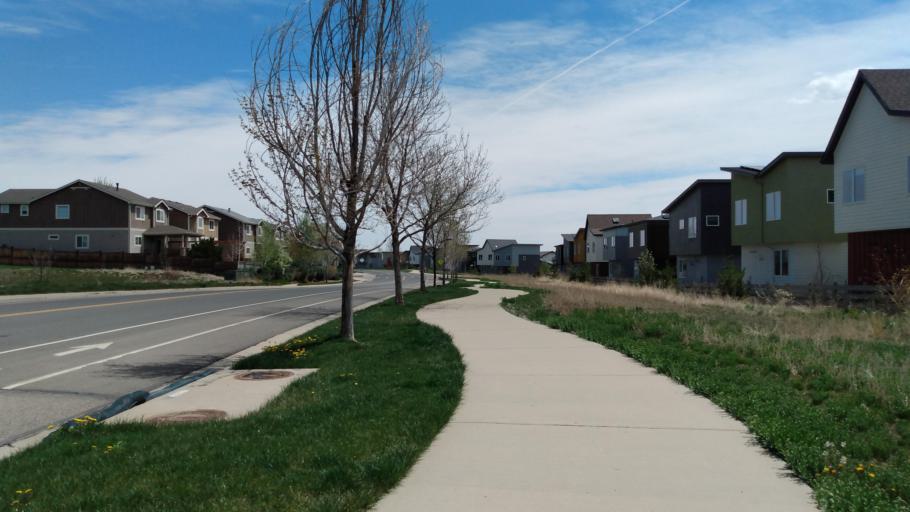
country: US
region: Colorado
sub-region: Boulder County
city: Lafayette
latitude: 40.0061
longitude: -105.0989
